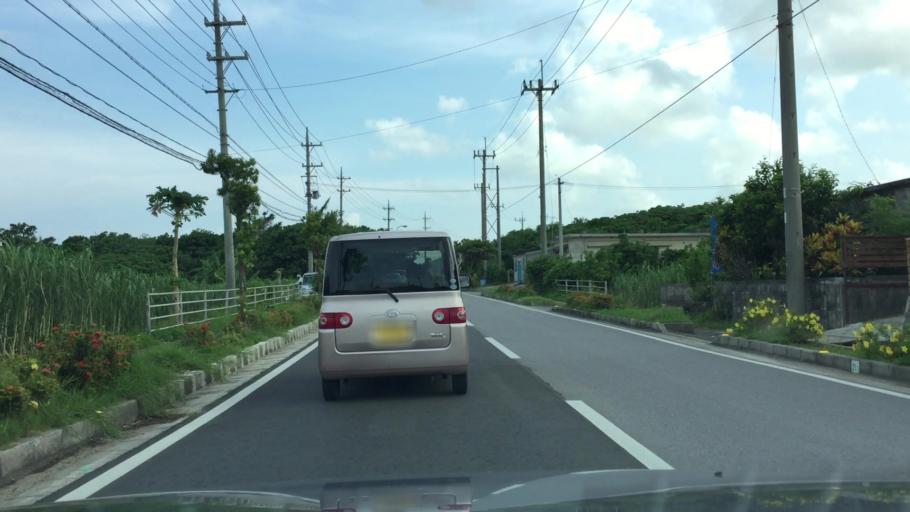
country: JP
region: Okinawa
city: Ishigaki
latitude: 24.4374
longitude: 124.2491
